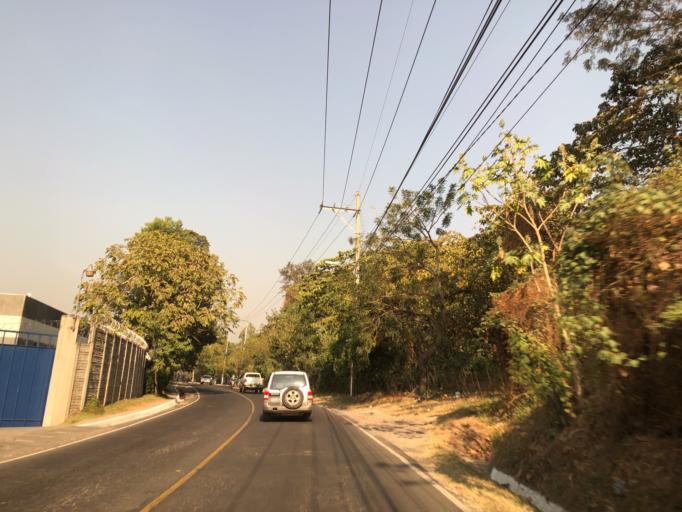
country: GT
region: Guatemala
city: Villa Canales
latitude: 14.4918
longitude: -90.5367
